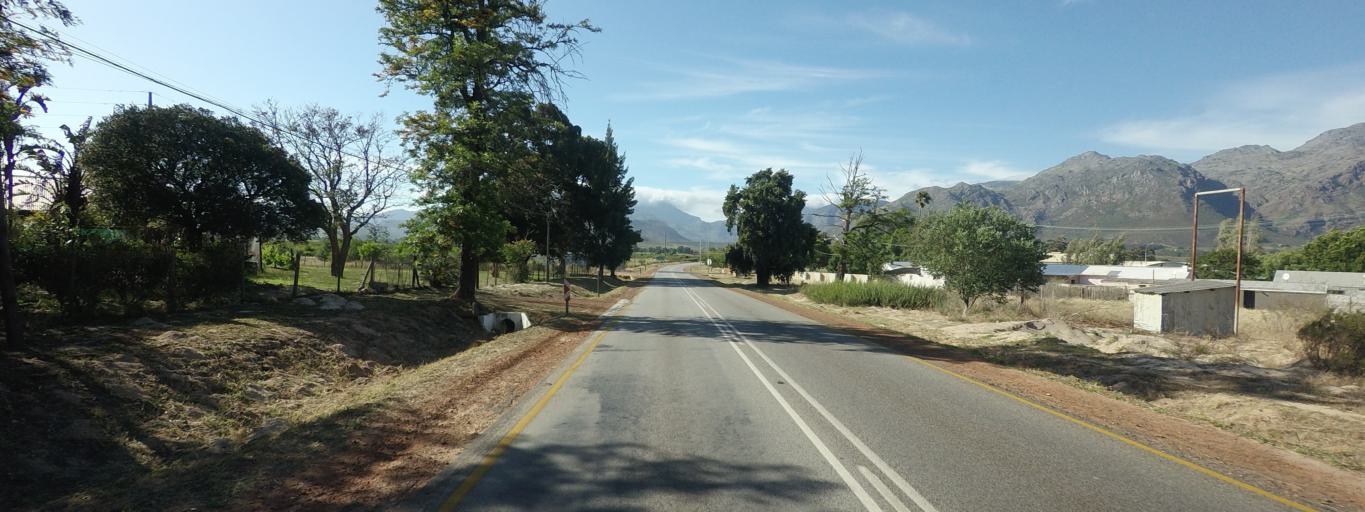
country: ZA
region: Western Cape
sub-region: Cape Winelands District Municipality
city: Paarl
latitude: -33.8708
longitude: 19.0435
